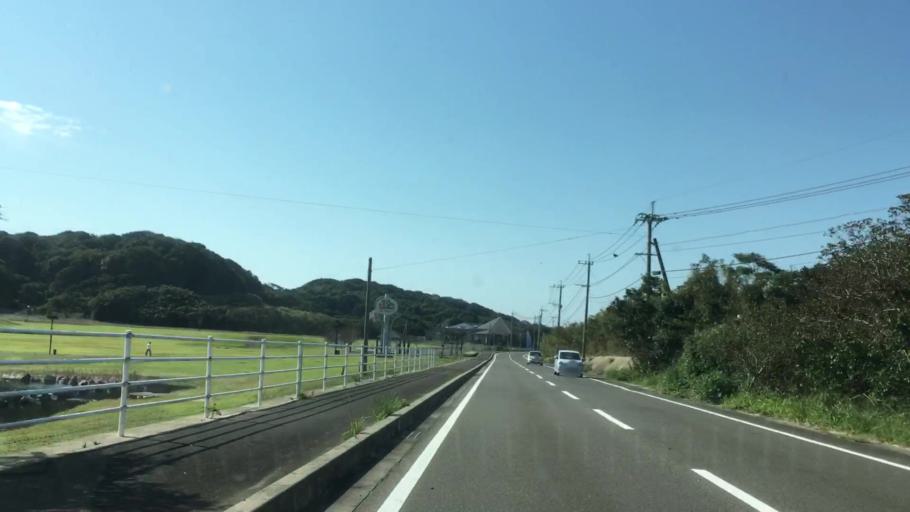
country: JP
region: Nagasaki
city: Sasebo
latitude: 33.0177
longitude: 129.5741
